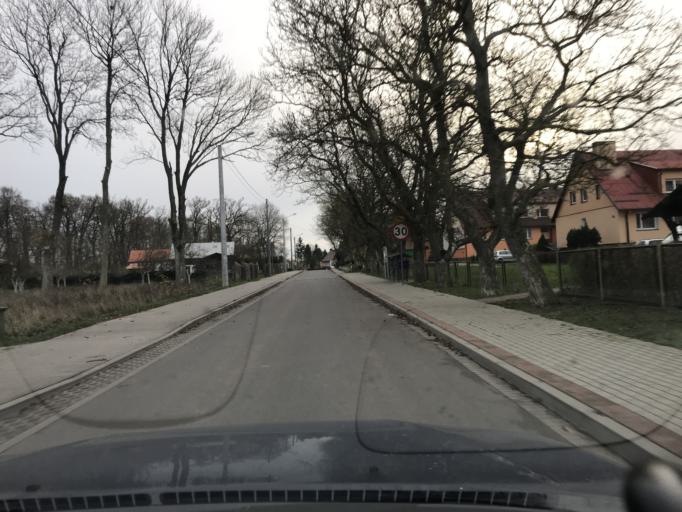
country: PL
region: Pomeranian Voivodeship
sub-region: Powiat slupski
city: Kobylnica
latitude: 54.4550
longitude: 16.8811
